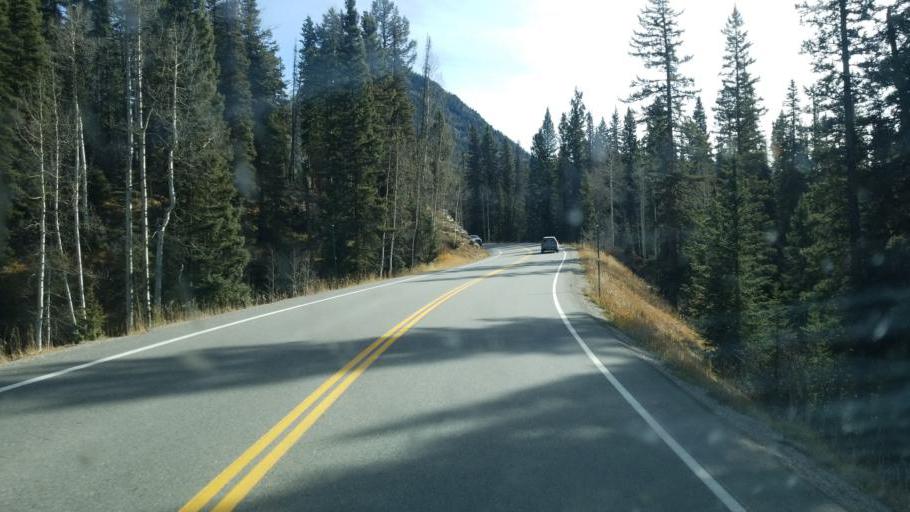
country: US
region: Colorado
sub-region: San Juan County
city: Silverton
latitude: 37.6733
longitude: -107.7930
